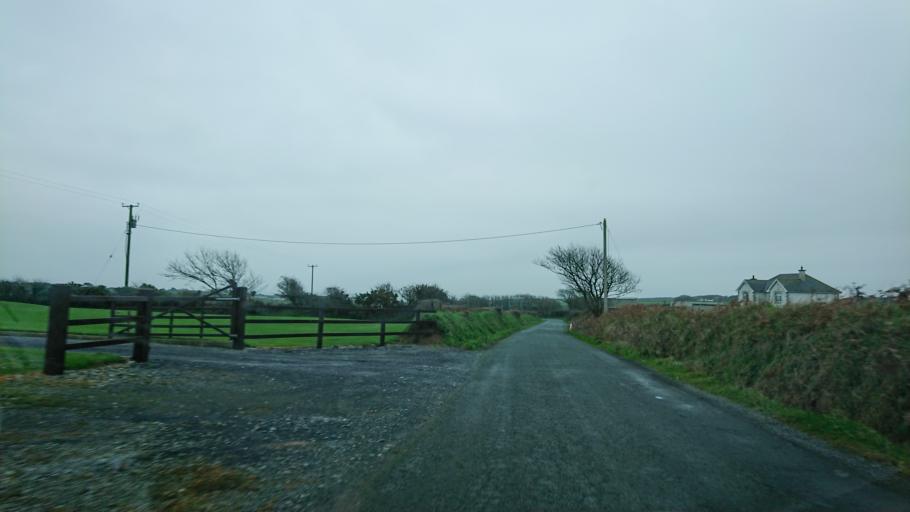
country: IE
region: Munster
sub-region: Waterford
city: Dunmore East
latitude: 52.1522
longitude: -7.0585
